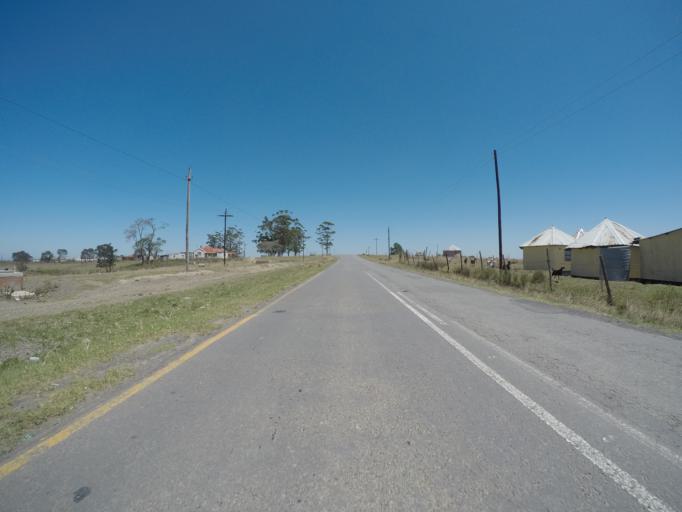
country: ZA
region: Eastern Cape
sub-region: OR Tambo District Municipality
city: Libode
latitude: -31.9169
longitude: 28.9803
